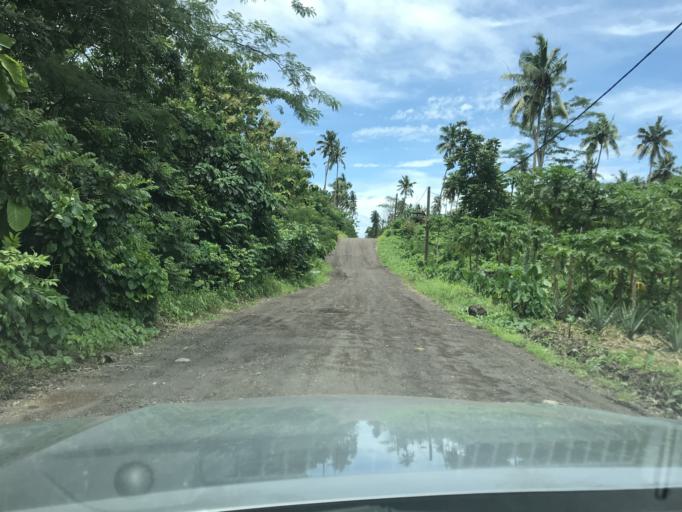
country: WS
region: Tuamasaga
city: Afenga
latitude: -13.8253
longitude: -171.8822
